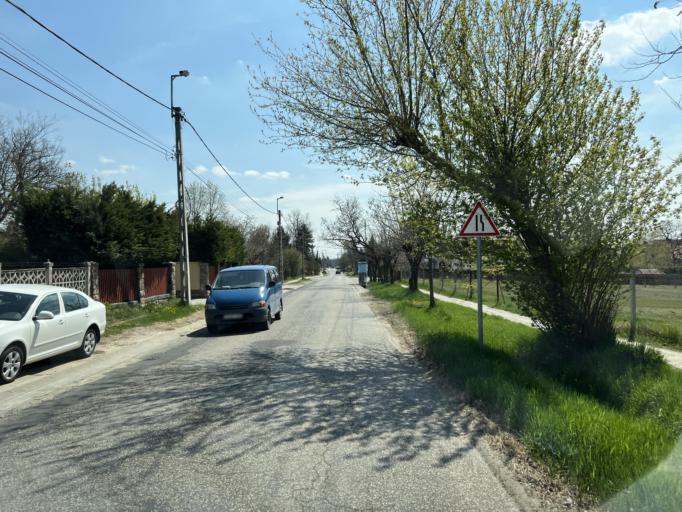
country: HU
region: Pest
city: Szada
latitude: 47.6237
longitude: 19.3397
